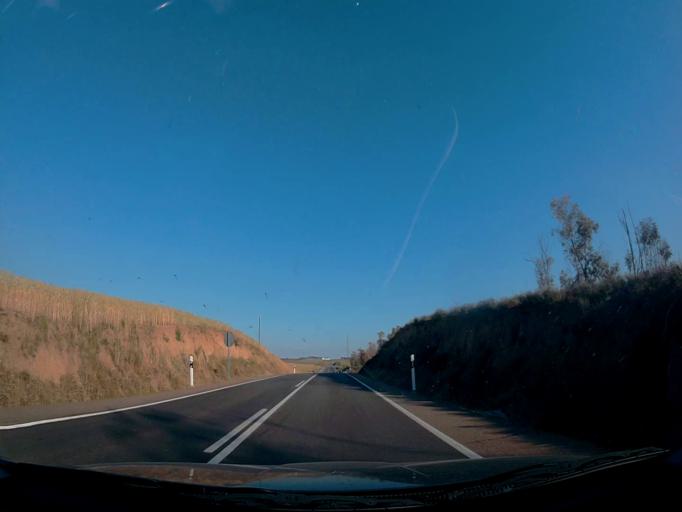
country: ES
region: Castille-La Mancha
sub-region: Province of Toledo
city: Hormigos
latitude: 40.1179
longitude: -4.4062
